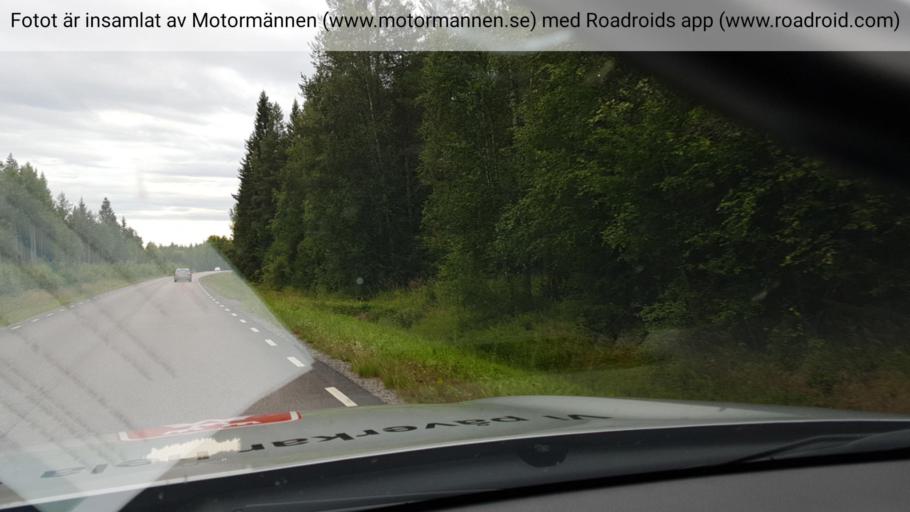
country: SE
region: Norrbotten
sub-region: Lulea Kommun
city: Gammelstad
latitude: 65.6559
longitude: 22.0380
